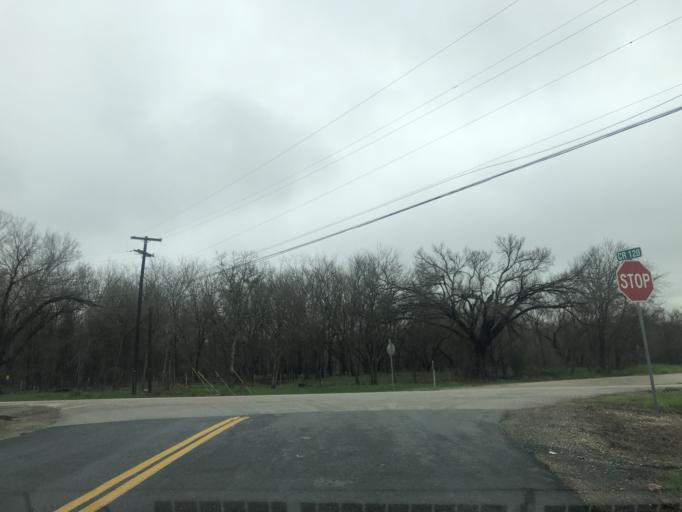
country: US
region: Texas
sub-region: Williamson County
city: Georgetown
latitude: 30.6470
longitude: -97.5827
